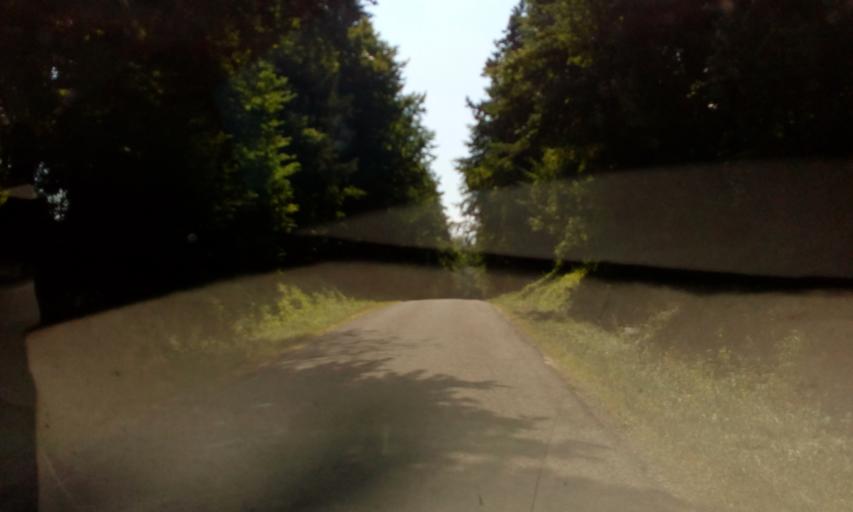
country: FR
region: Lorraine
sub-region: Departement de la Meuse
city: Verdun
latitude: 49.2224
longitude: 5.4787
